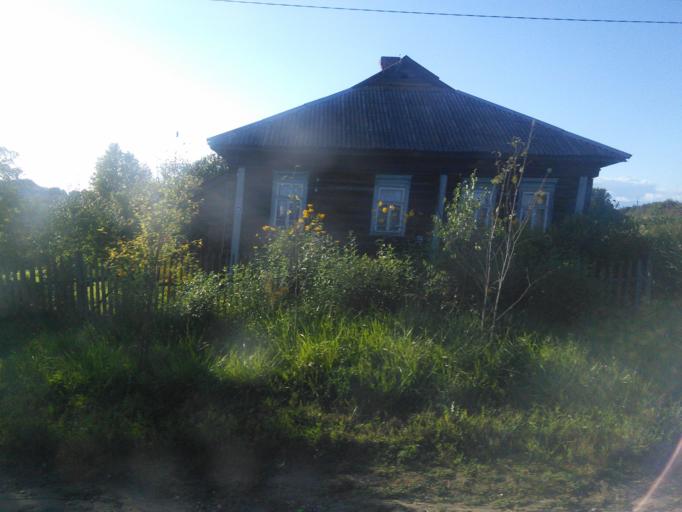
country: RU
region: Jaroslavl
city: Poshekhon'ye
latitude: 58.4274
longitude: 38.9989
